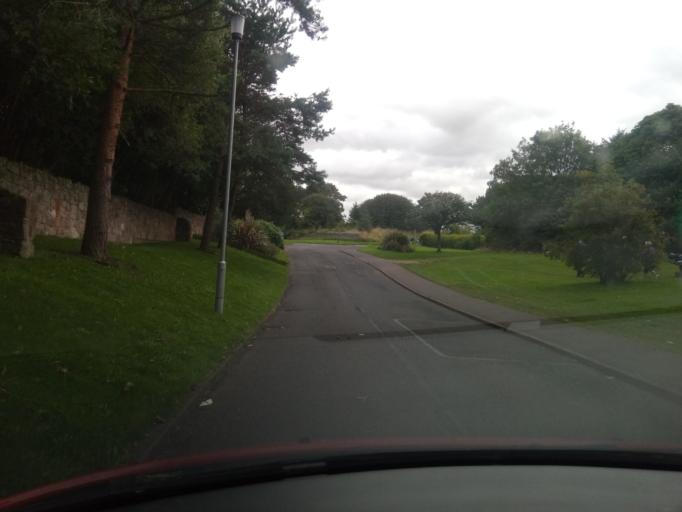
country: GB
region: England
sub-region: Northumberland
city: Berwick-Upon-Tweed
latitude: 55.7770
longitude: -2.0035
